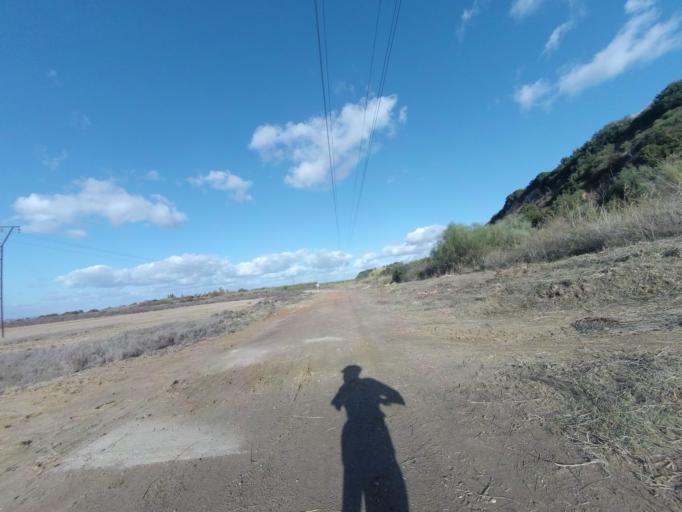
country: ES
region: Andalusia
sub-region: Provincia de Huelva
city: Palos de la Frontera
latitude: 37.2537
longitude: -6.8771
